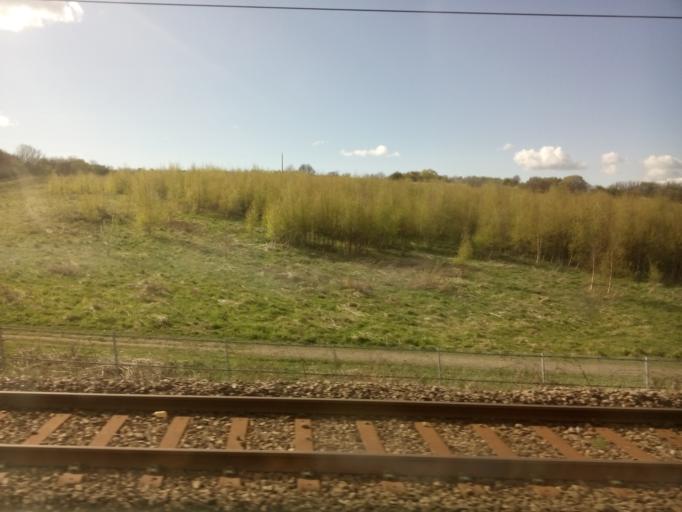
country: GB
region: England
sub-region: County Durham
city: Durham
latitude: 54.7880
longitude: -1.5739
